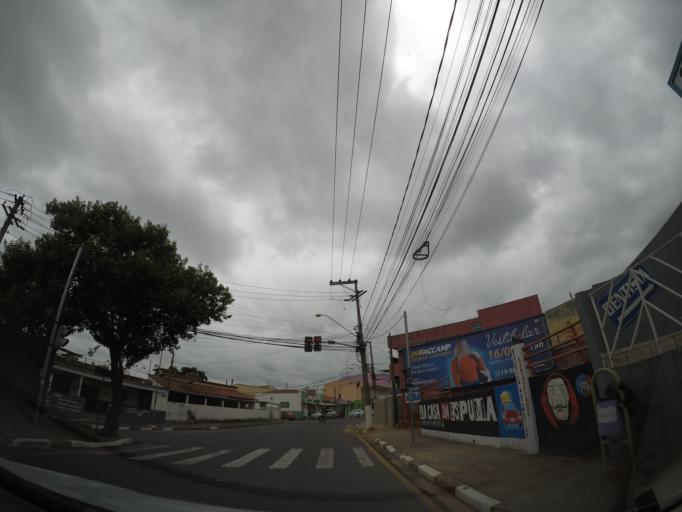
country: BR
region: Sao Paulo
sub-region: Louveira
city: Louveira
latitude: -23.0861
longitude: -46.9801
